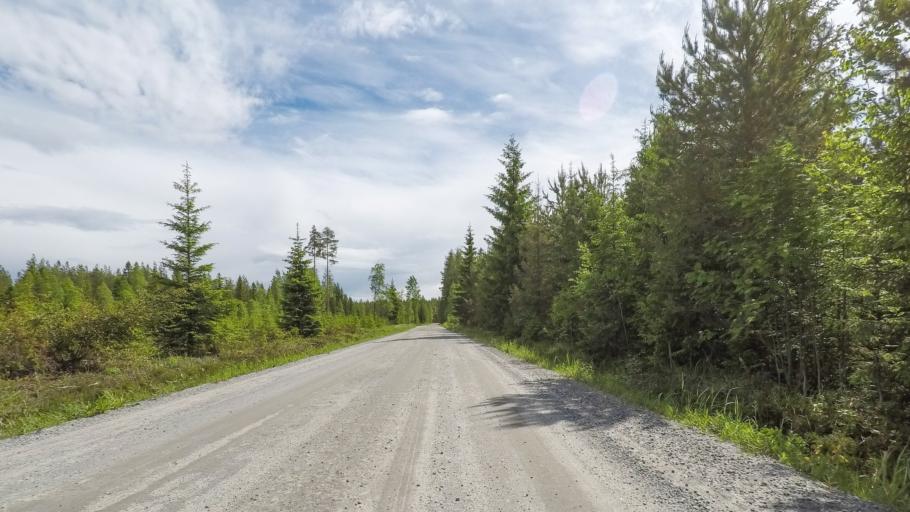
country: FI
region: Central Finland
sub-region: Jyvaeskylae
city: Hankasalmi
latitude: 62.3953
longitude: 26.5964
